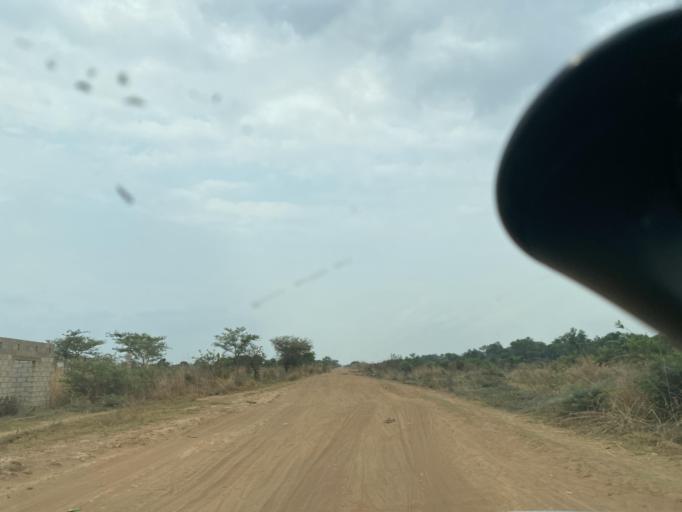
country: ZM
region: Lusaka
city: Lusaka
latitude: -15.2087
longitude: 28.3398
